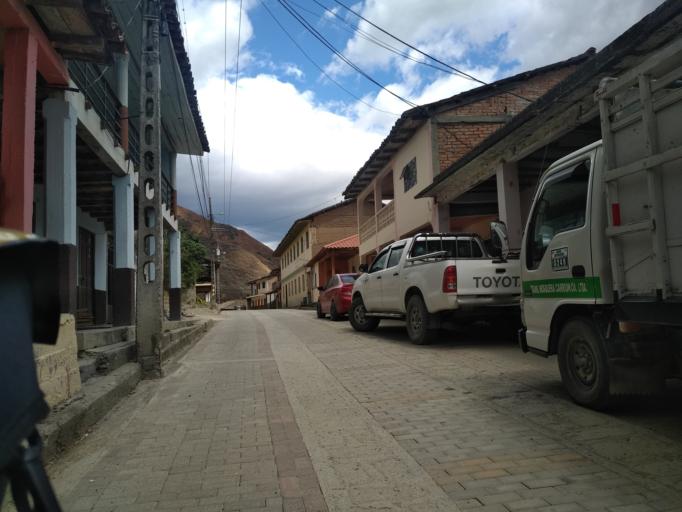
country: EC
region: Loja
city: Loja
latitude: -4.2423
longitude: -79.2225
